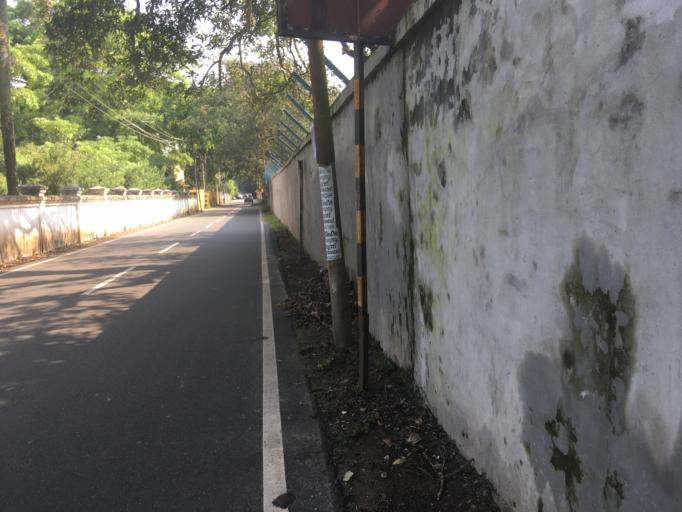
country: IN
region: Kerala
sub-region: Ernakulam
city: Cochin
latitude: 9.9611
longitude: 76.2379
